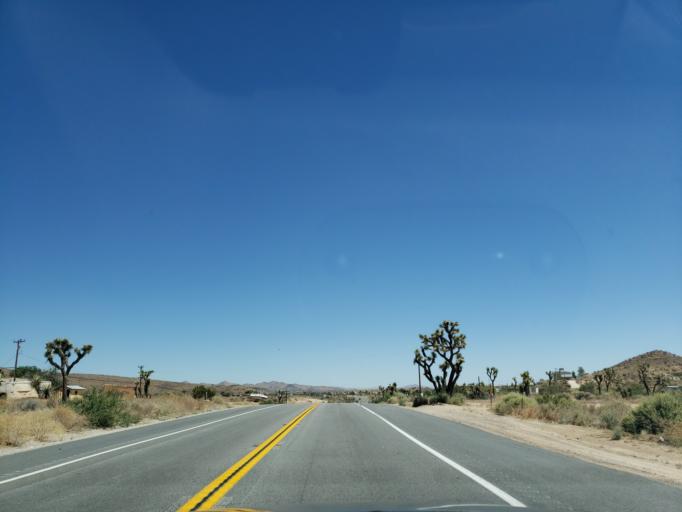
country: US
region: California
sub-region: San Bernardino County
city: Yucca Valley
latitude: 34.1686
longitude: -116.4240
